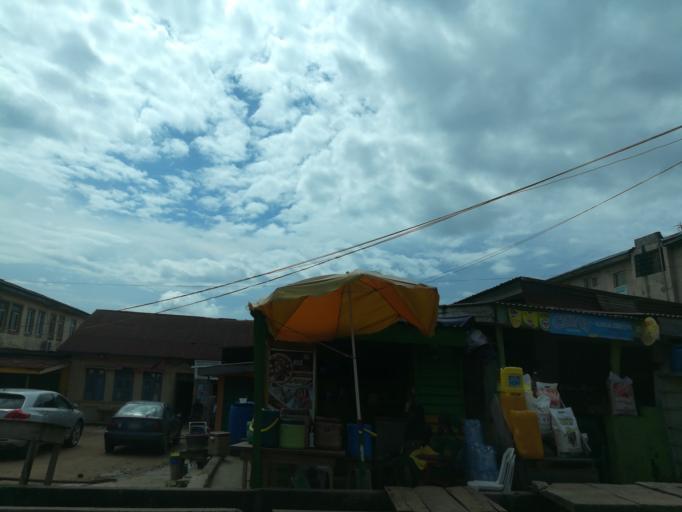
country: NG
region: Lagos
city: Ikorodu
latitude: 6.6142
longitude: 3.5017
